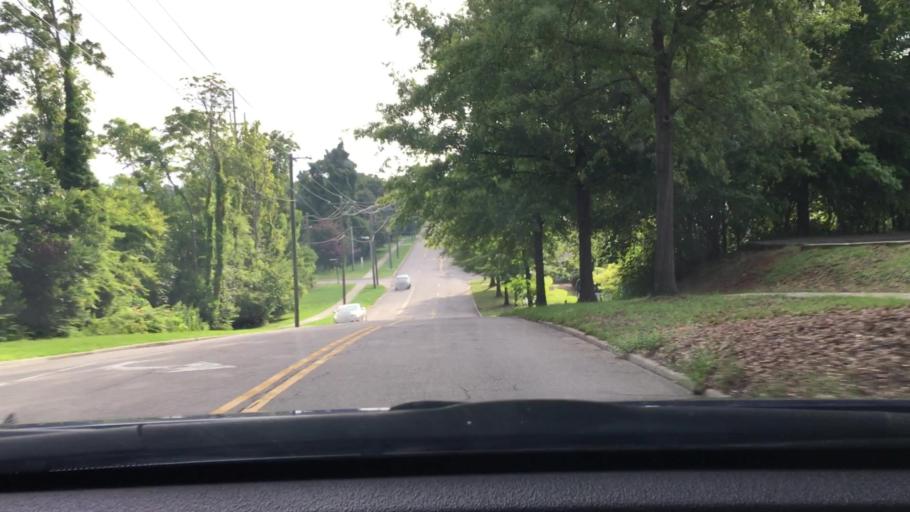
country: US
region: South Carolina
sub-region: Richland County
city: Columbia
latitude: 34.0150
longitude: -81.0284
